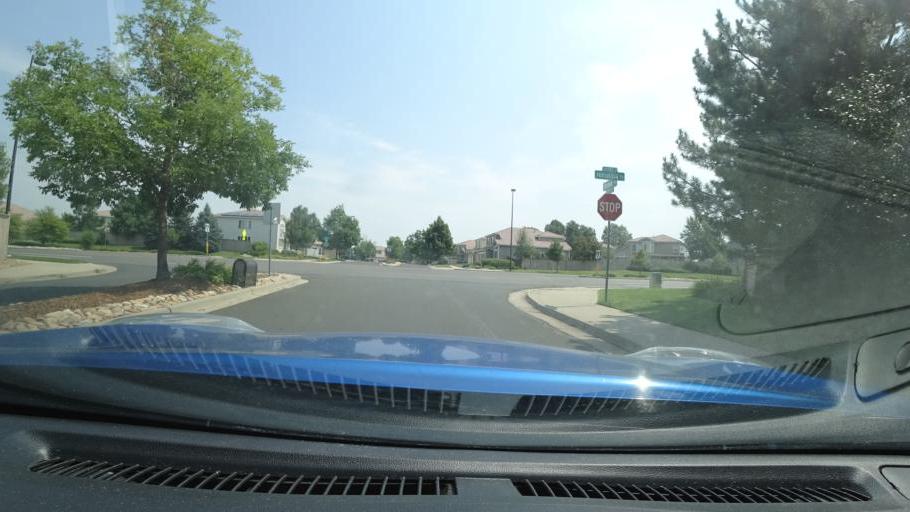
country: US
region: Colorado
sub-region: Adams County
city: Aurora
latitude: 39.7771
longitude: -104.7543
